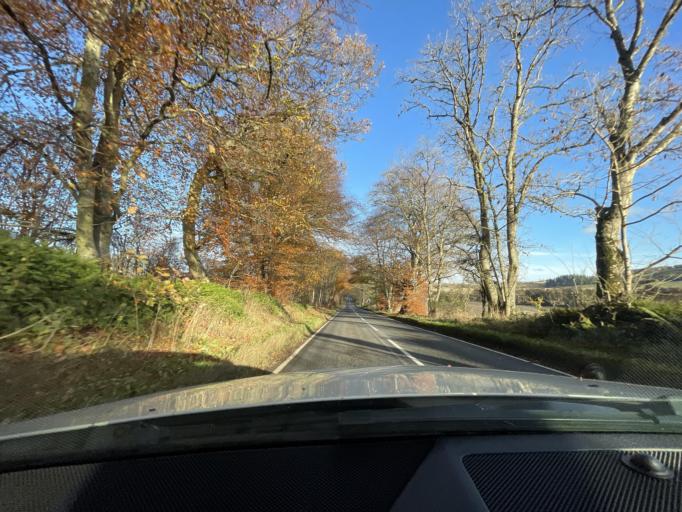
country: GB
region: Scotland
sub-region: Highland
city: Inverness
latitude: 57.4266
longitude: -4.2872
